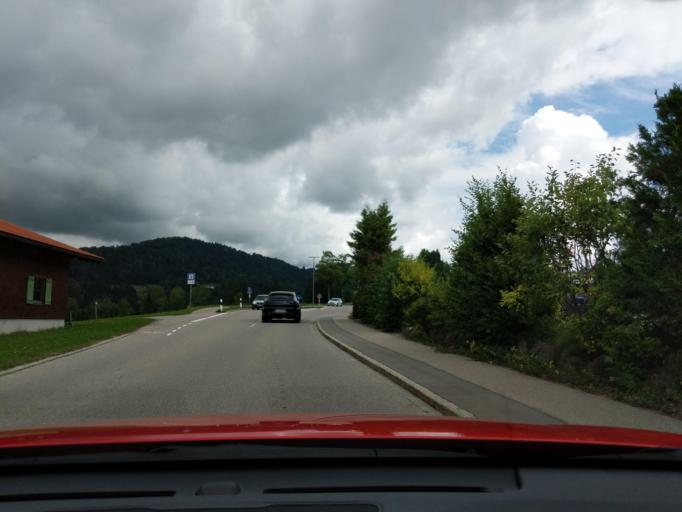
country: AT
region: Vorarlberg
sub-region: Politischer Bezirk Bregenz
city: Riefensberg
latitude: 47.5227
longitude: 9.9726
